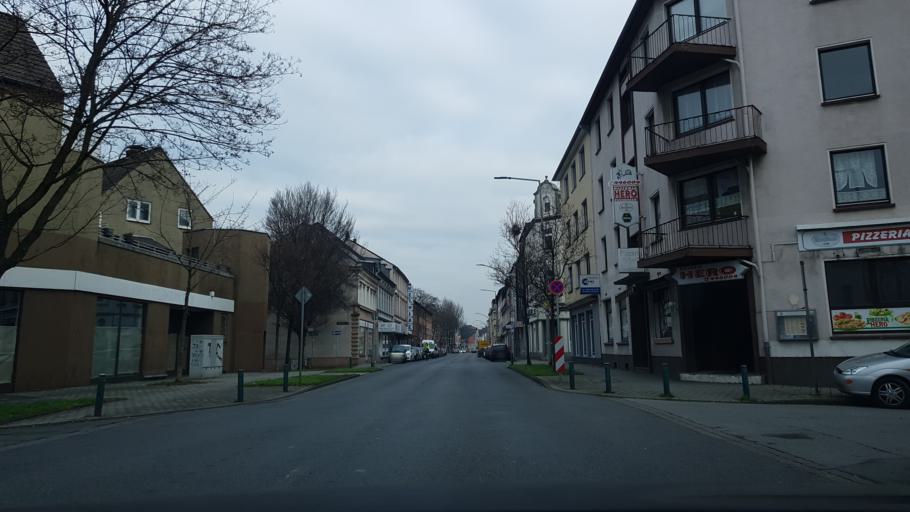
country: DE
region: North Rhine-Westphalia
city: Meiderich
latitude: 51.4638
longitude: 6.7599
